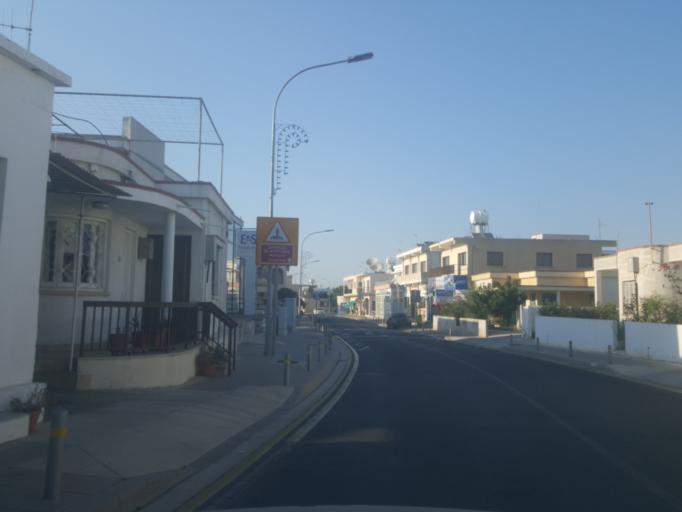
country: CY
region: Ammochostos
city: Deryneia
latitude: 35.0640
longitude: 33.9609
